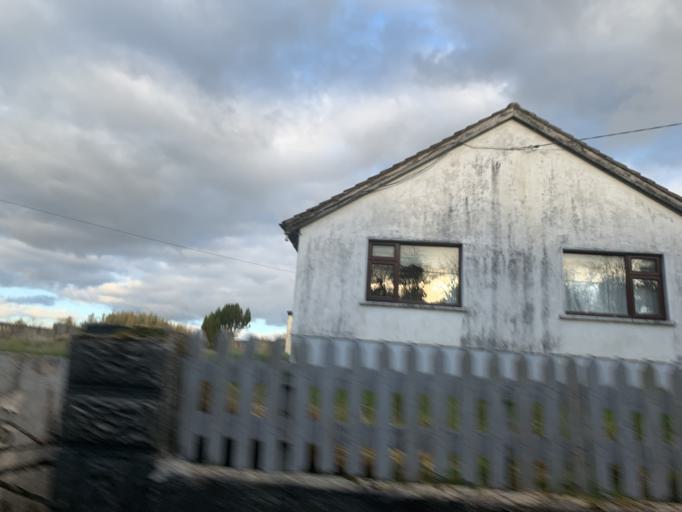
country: IE
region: Connaught
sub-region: Maigh Eo
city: Ballyhaunis
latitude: 53.8302
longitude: -8.7044
